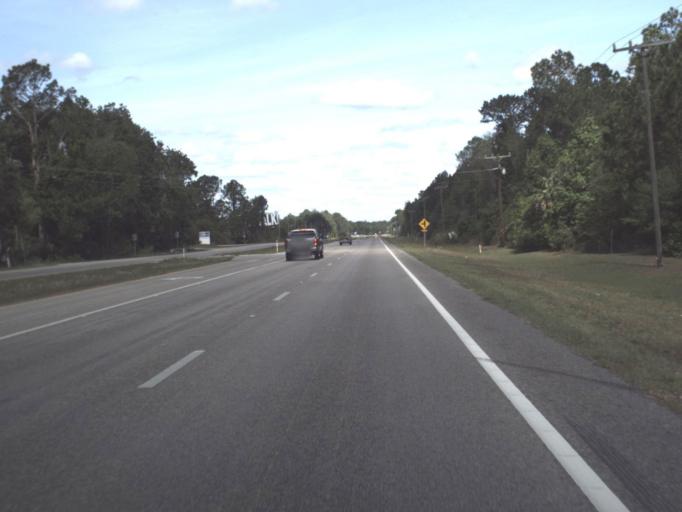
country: US
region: Florida
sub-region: Flagler County
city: Bunnell
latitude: 29.4261
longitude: -81.2211
